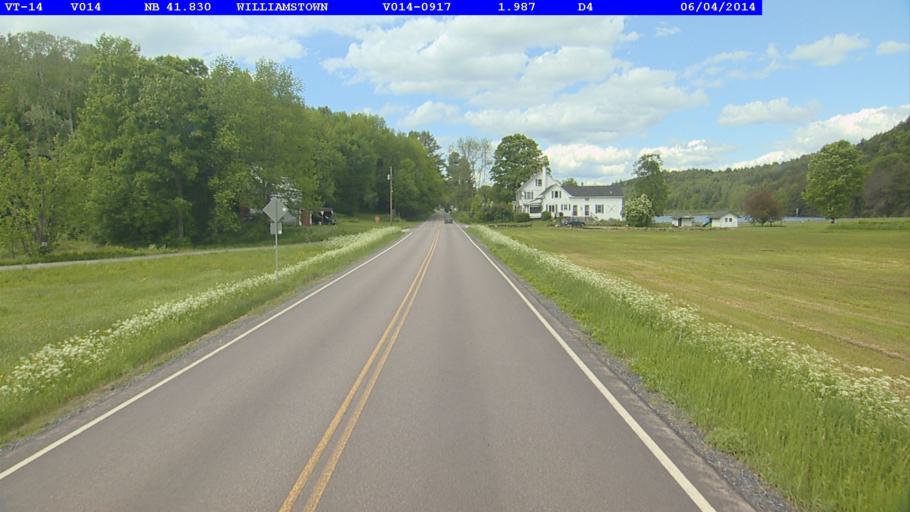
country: US
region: Vermont
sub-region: Orange County
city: Williamstown
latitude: 44.0882
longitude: -72.5522
